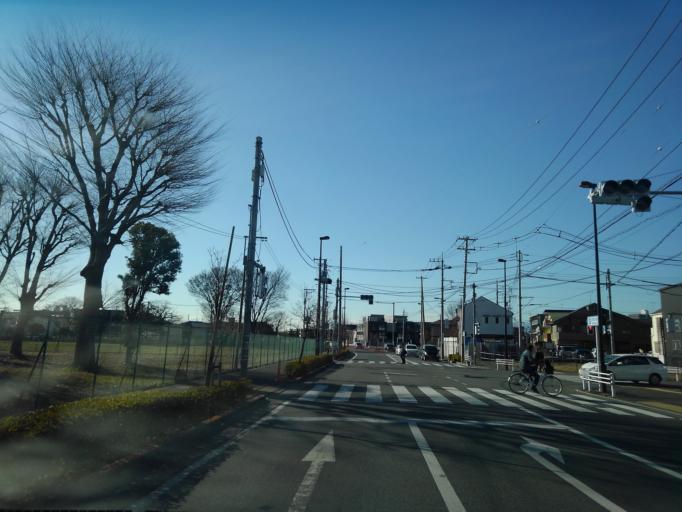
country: JP
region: Tokyo
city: Hino
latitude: 35.7111
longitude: 139.3790
